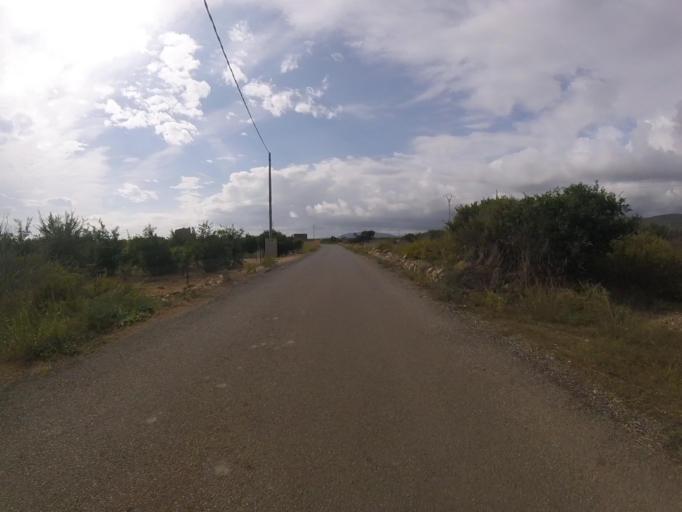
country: ES
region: Valencia
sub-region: Provincia de Castello
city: Torreblanca
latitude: 40.1751
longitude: 0.1714
